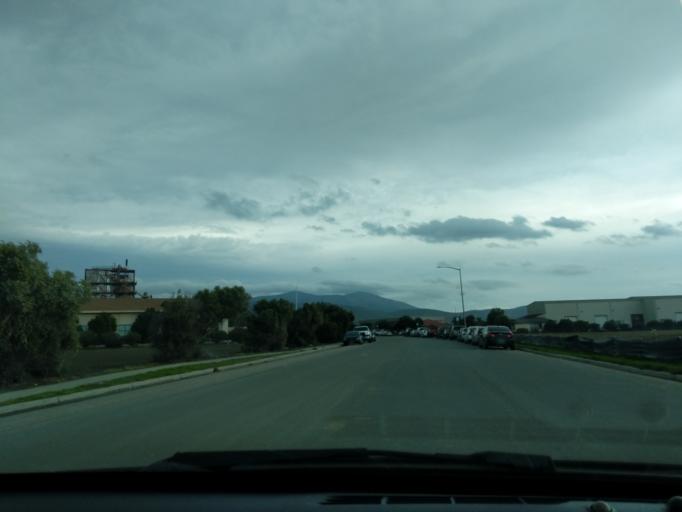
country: US
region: California
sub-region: Monterey County
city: Soledad
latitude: 36.4150
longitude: -121.3184
